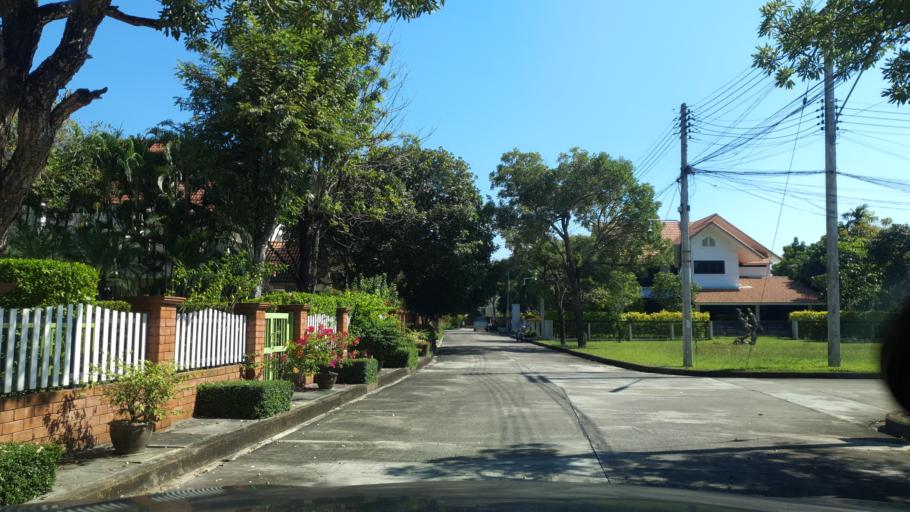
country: TH
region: Chiang Mai
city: Hang Dong
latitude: 18.7337
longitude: 98.9438
